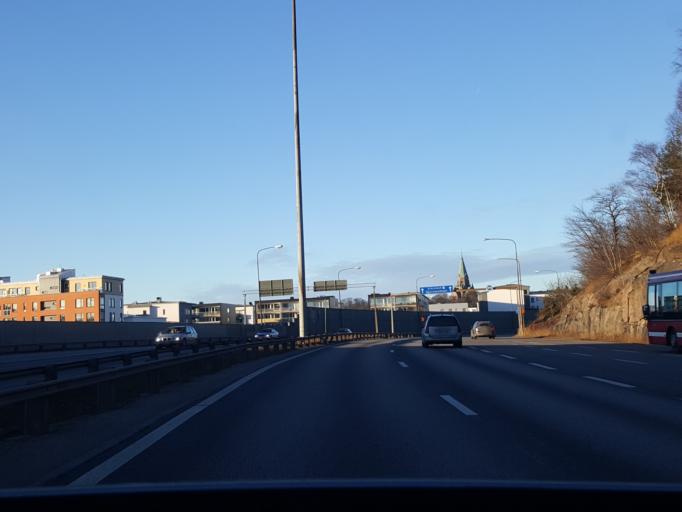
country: SE
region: Stockholm
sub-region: Stockholms Kommun
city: OEstermalm
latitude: 59.3082
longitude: 18.1093
